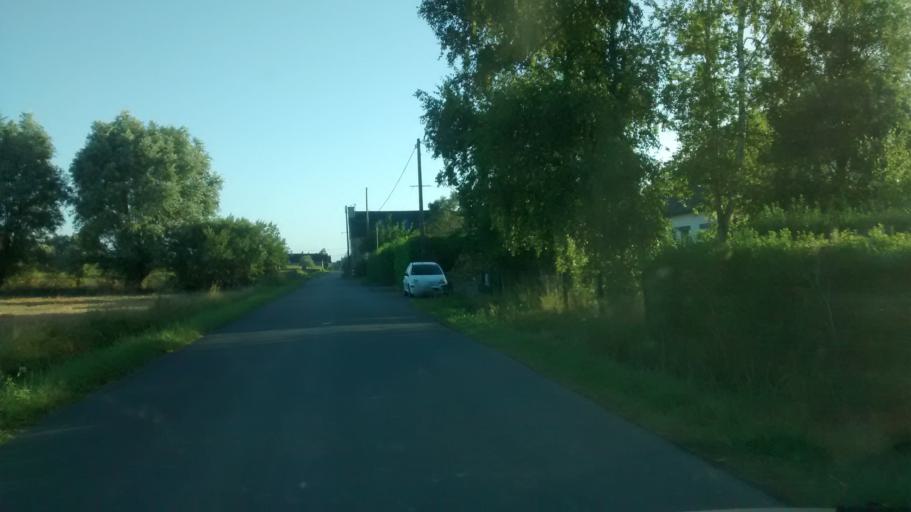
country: FR
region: Brittany
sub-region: Departement d'Ille-et-Vilaine
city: La Fresnais
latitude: 48.5835
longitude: -1.8615
